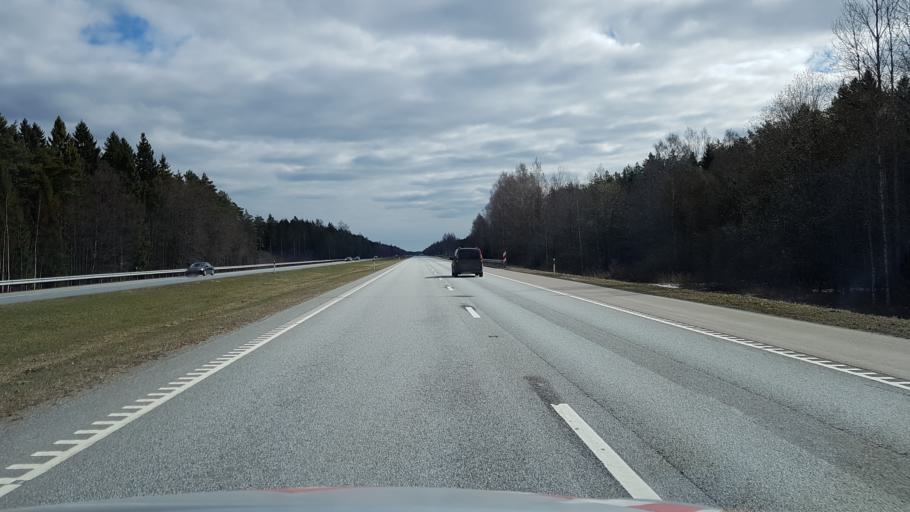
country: EE
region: Harju
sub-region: Kuusalu vald
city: Kuusalu
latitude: 59.4576
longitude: 25.5453
